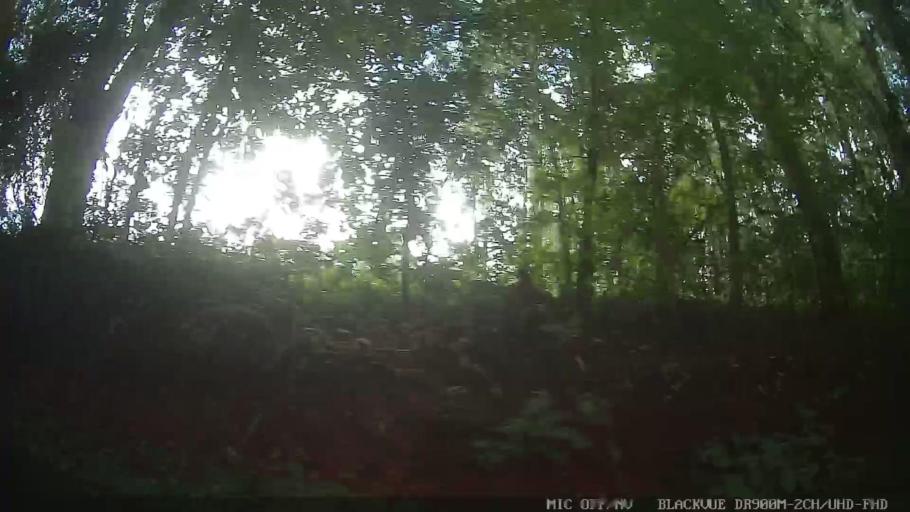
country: BR
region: Sao Paulo
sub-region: Braganca Paulista
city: Braganca Paulista
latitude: -23.0263
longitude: -46.4702
